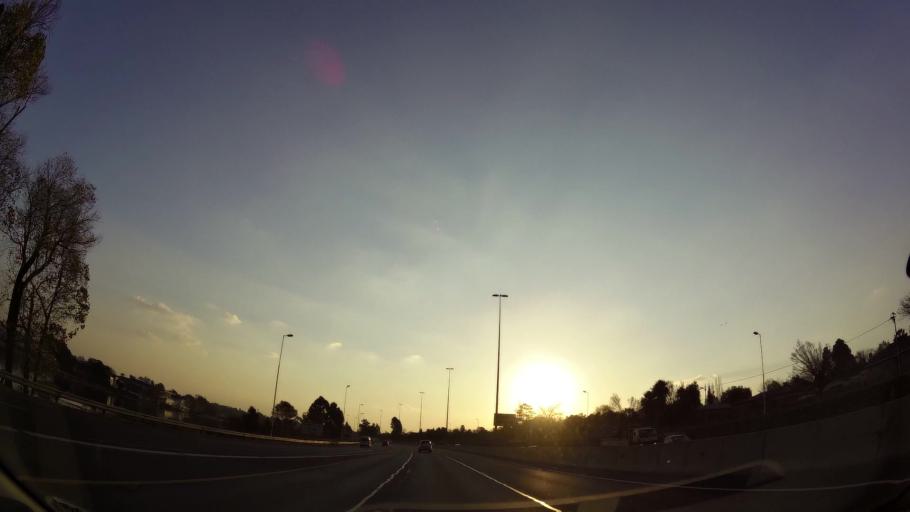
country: ZA
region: Gauteng
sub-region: Ekurhuleni Metropolitan Municipality
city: Benoni
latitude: -26.1811
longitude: 28.3075
